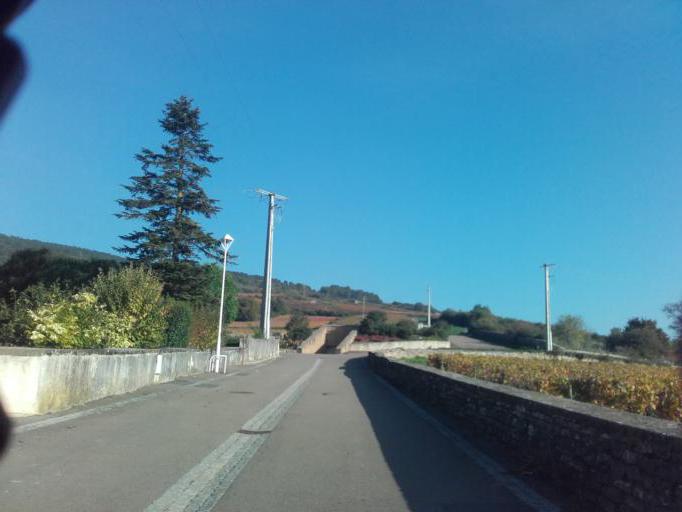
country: FR
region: Bourgogne
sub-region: Departement de Saone-et-Loire
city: Chagny
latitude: 46.9132
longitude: 4.7012
